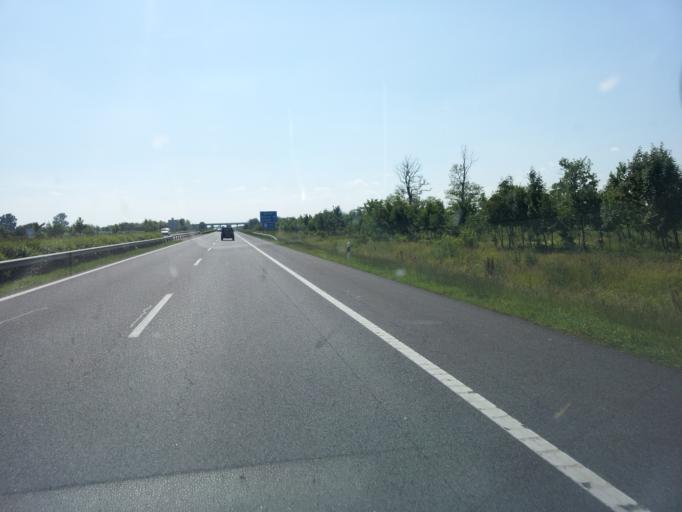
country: HU
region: Borsod-Abauj-Zemplen
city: Emod
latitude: 47.8722
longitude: 20.7995
